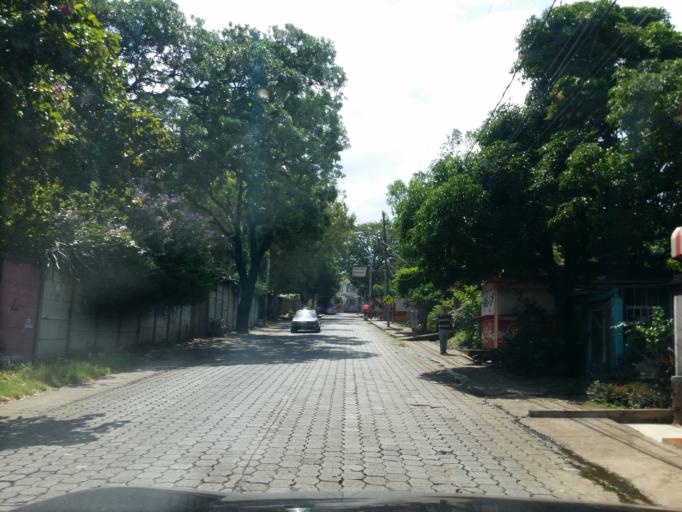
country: NI
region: Managua
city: Managua
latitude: 12.1206
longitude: -86.2758
